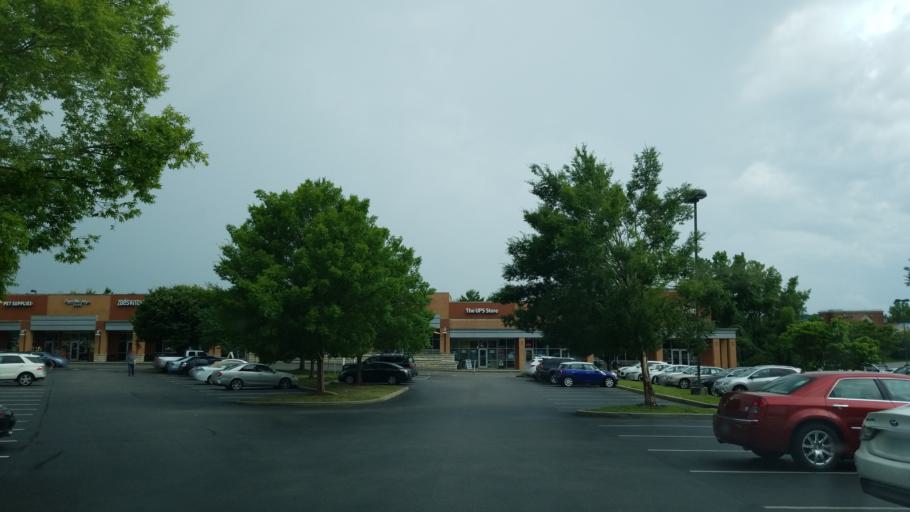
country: US
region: Tennessee
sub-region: Williamson County
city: Brentwood
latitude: 36.0377
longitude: -86.8001
